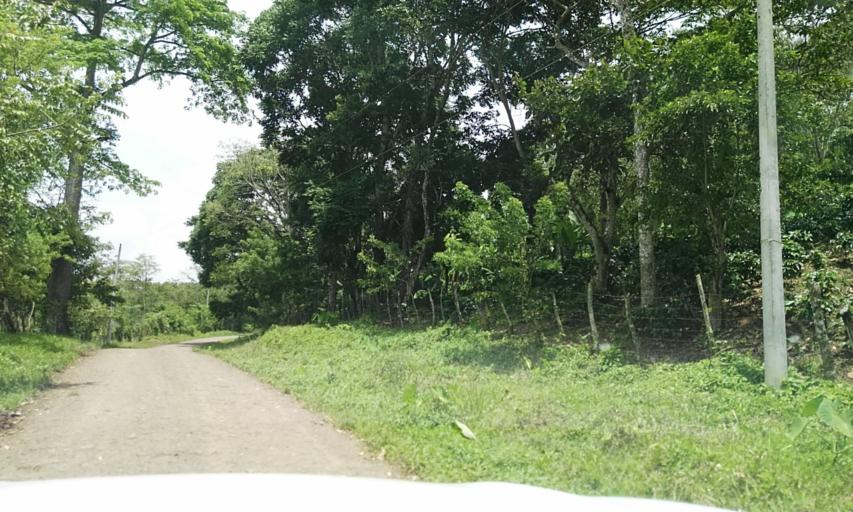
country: NI
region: Matagalpa
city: San Ramon
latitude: 12.9878
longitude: -85.8540
